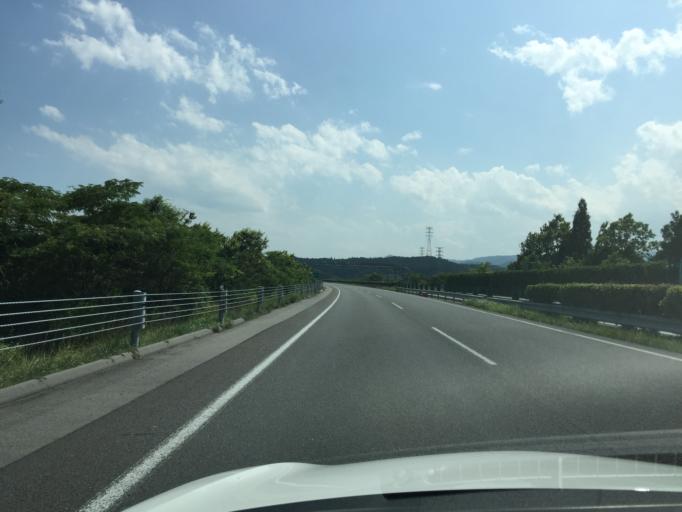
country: JP
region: Ibaraki
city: Kitaibaraki
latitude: 36.9262
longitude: 140.7624
